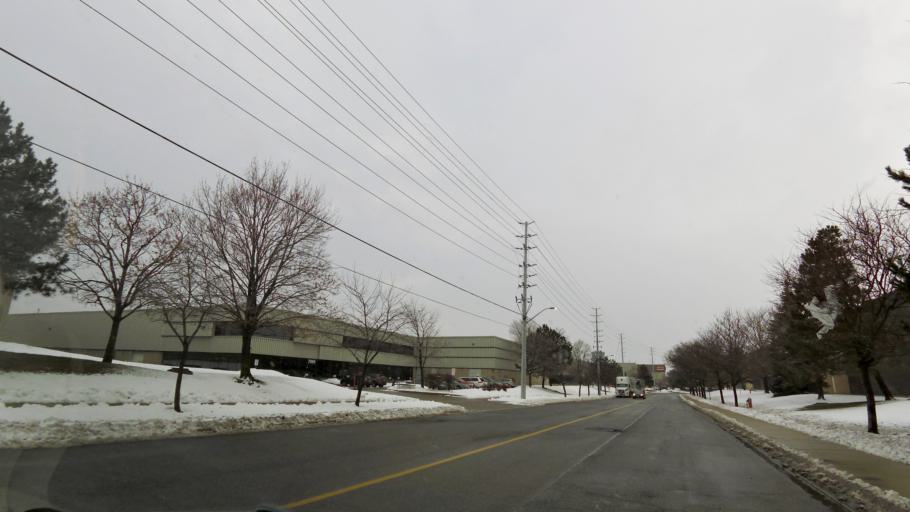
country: CA
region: Ontario
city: Mississauga
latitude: 43.6583
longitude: -79.6668
